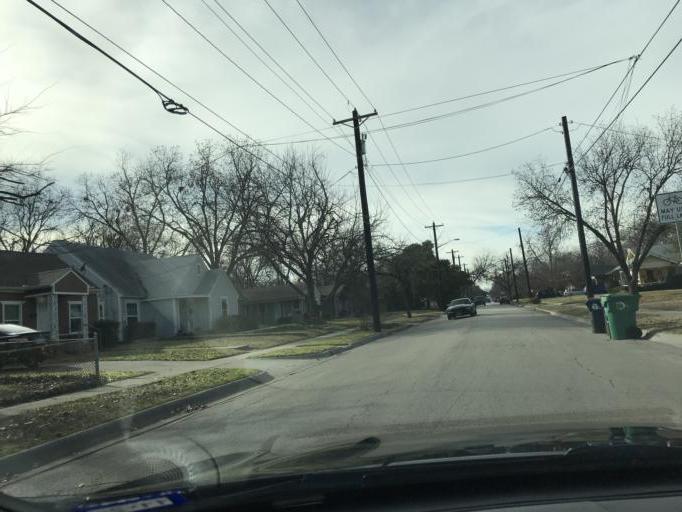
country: US
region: Texas
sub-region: Denton County
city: Denton
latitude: 33.2214
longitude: -97.1404
